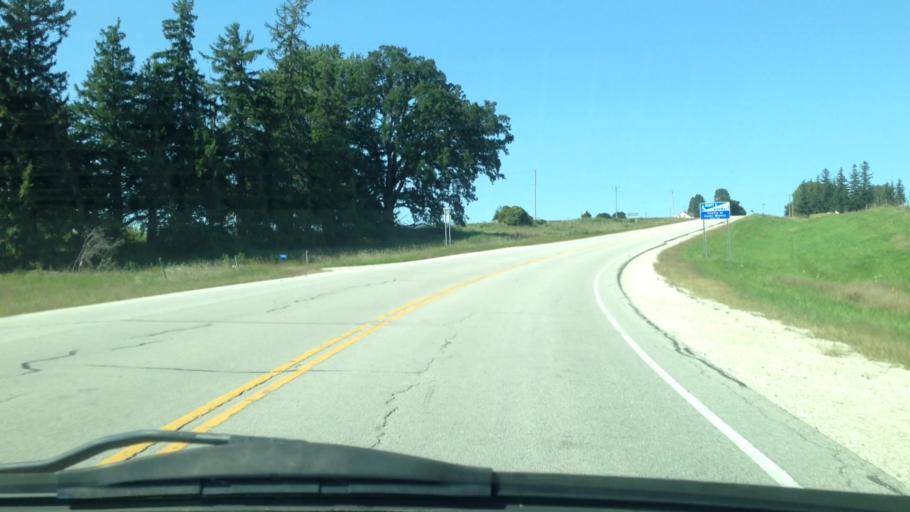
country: US
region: Minnesota
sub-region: Houston County
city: Spring Grove
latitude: 43.6033
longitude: -91.7899
